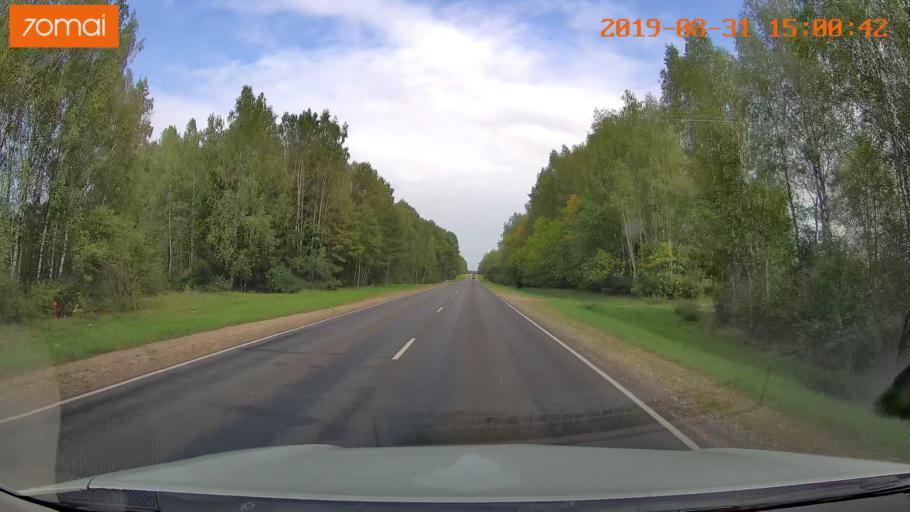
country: RU
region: Kaluga
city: Spas-Demensk
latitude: 54.3340
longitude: 34.0381
